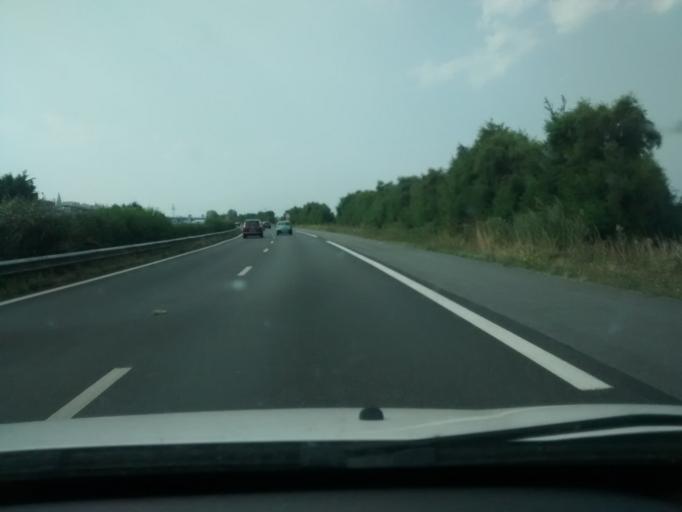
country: FR
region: Pays de la Loire
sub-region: Departement de la Loire-Atlantique
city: Saint-Nazaire
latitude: 47.3025
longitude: -2.2141
